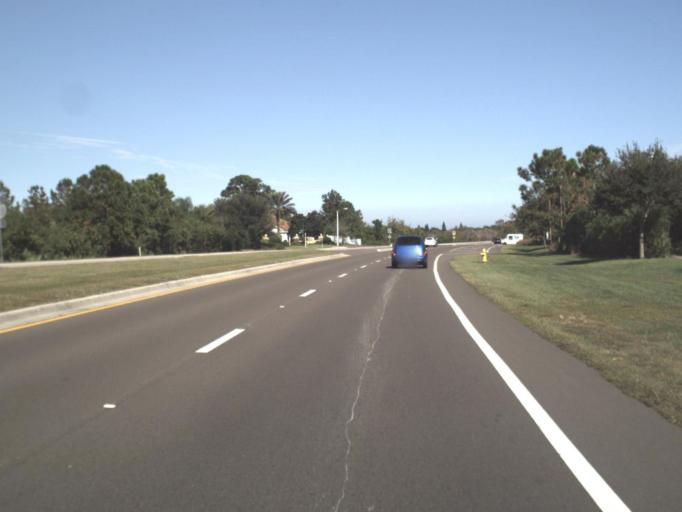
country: US
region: Florida
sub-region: Brevard County
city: South Patrick Shores
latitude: 28.1978
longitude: -80.6878
